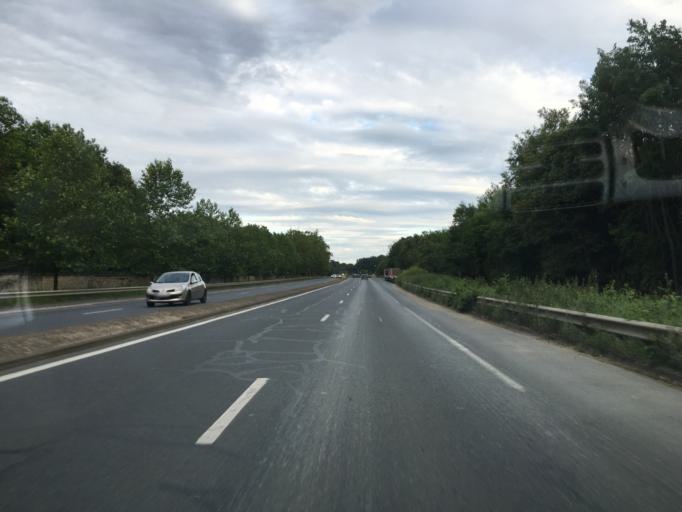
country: FR
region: Ile-de-France
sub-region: Departement du Val-de-Marne
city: Boissy-Saint-Leger
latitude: 48.7393
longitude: 2.5161
